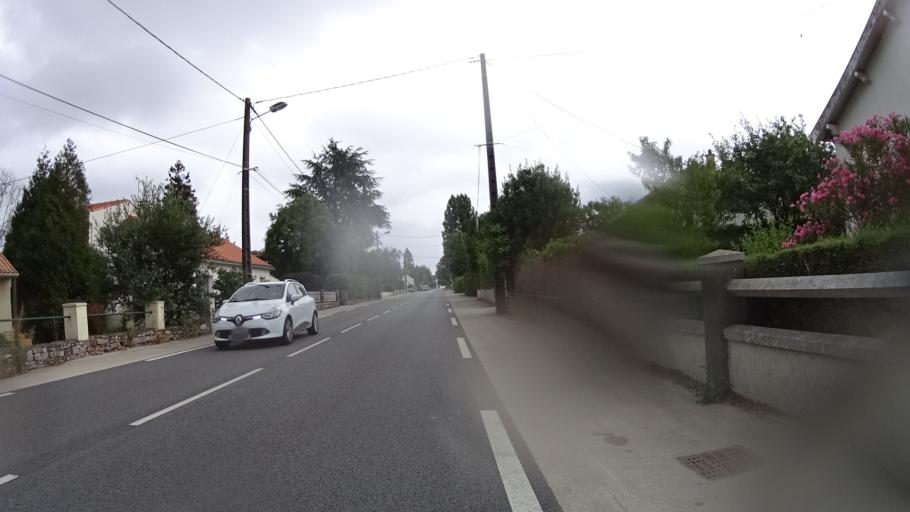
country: FR
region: Pays de la Loire
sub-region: Departement de la Loire-Atlantique
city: Indre
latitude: 47.1785
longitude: -1.6513
